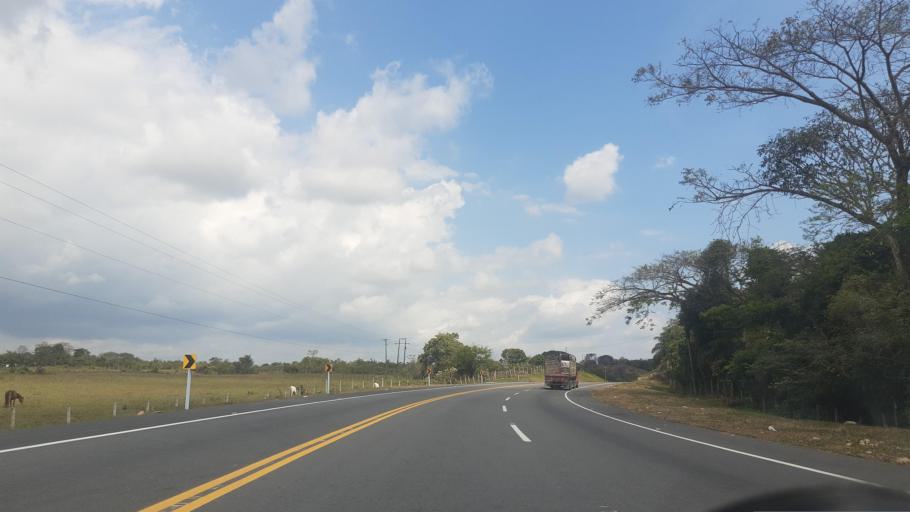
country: CO
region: Casanare
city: Tauramena
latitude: 4.9326
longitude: -72.6713
